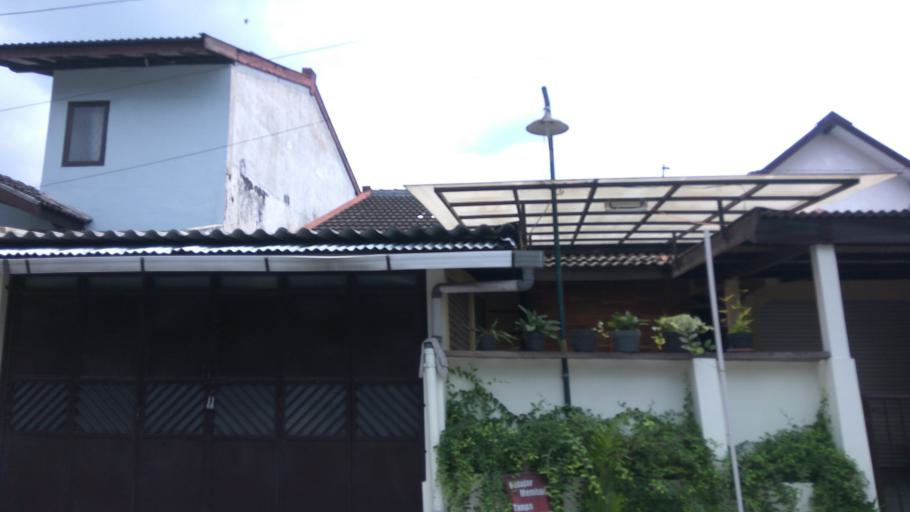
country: ID
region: Daerah Istimewa Yogyakarta
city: Depok
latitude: -7.7421
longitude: 110.4079
